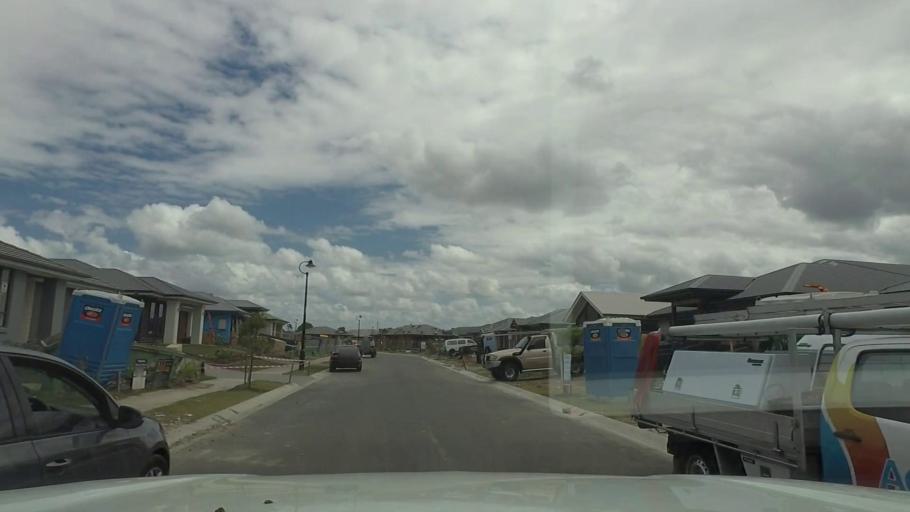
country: AU
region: Queensland
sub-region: Logan
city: Logan Reserve
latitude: -27.7185
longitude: 153.1167
